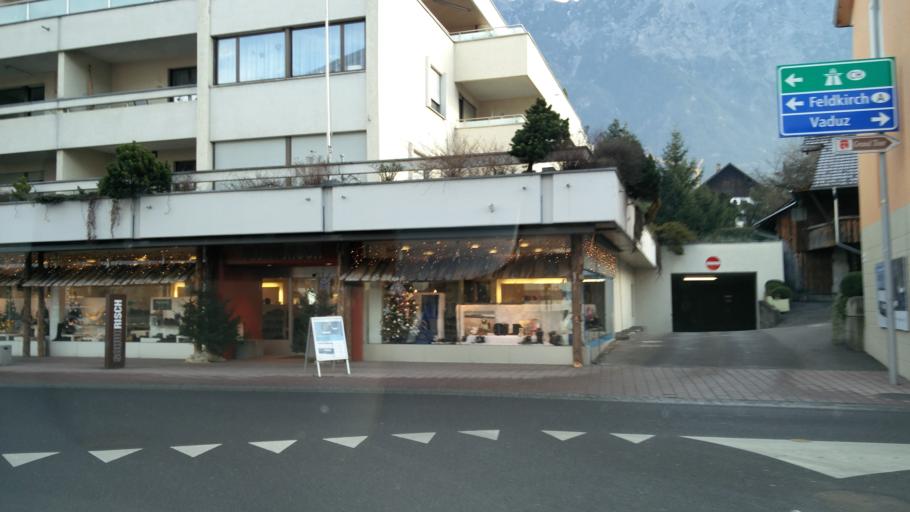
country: LI
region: Schaan
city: Schaan
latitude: 47.1652
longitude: 9.5087
